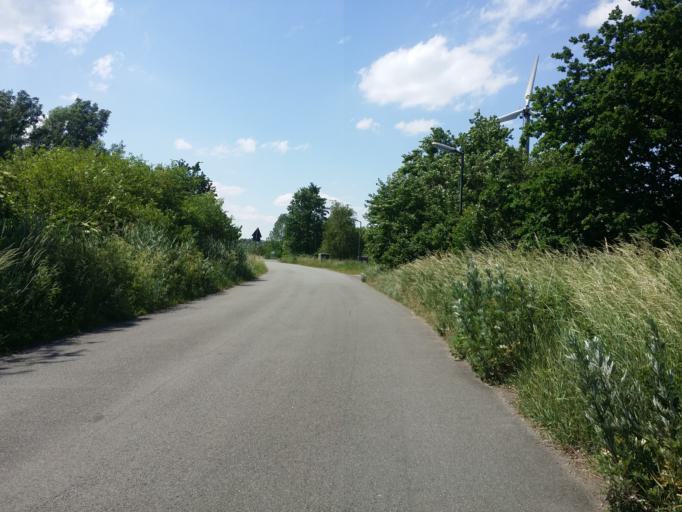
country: DE
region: Lower Saxony
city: Lemwerder
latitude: 53.1212
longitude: 8.6703
